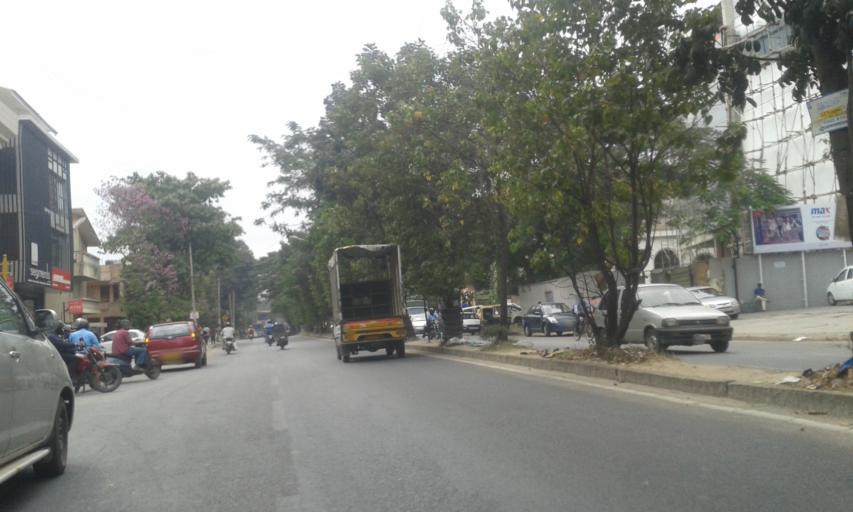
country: IN
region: Karnataka
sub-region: Bangalore Urban
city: Bangalore
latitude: 12.9067
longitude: 77.5985
